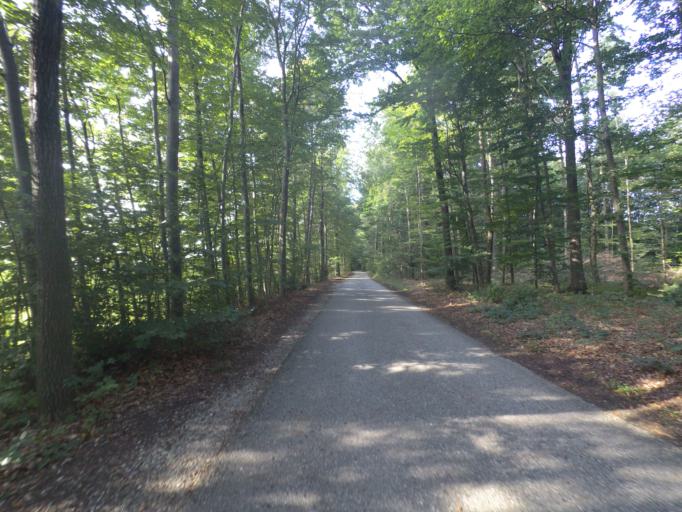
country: DE
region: Bavaria
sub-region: Upper Bavaria
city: Laufen
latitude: 47.9071
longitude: 12.9019
